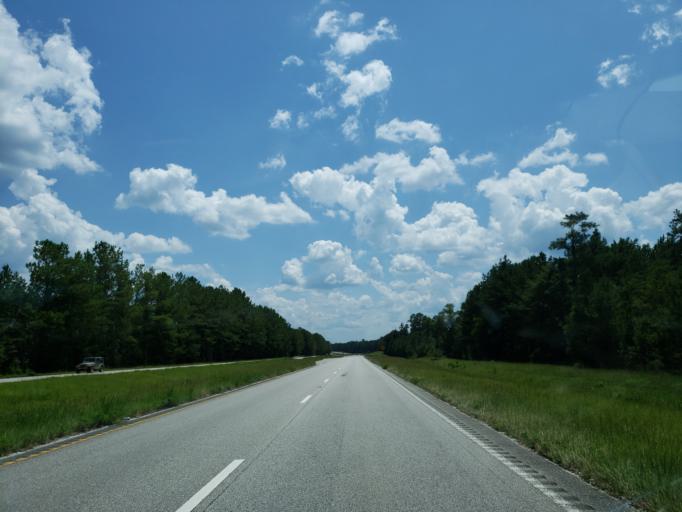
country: US
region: Mississippi
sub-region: Greene County
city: Leakesville
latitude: 31.3345
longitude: -88.5047
